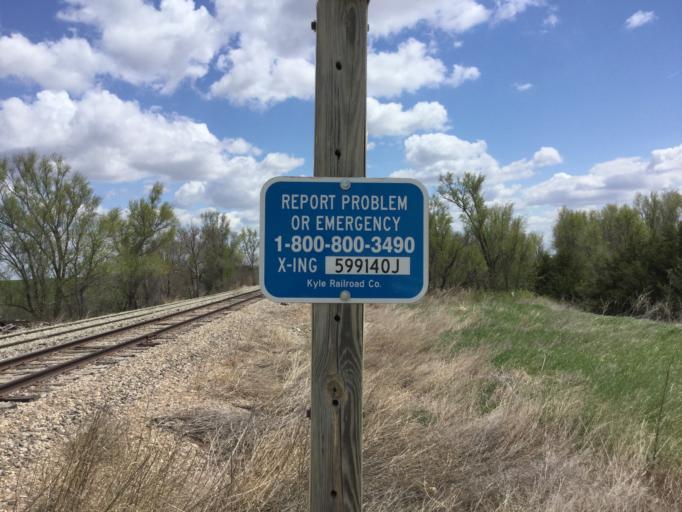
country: US
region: Kansas
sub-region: Phillips County
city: Phillipsburg
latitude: 39.7638
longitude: -99.1136
